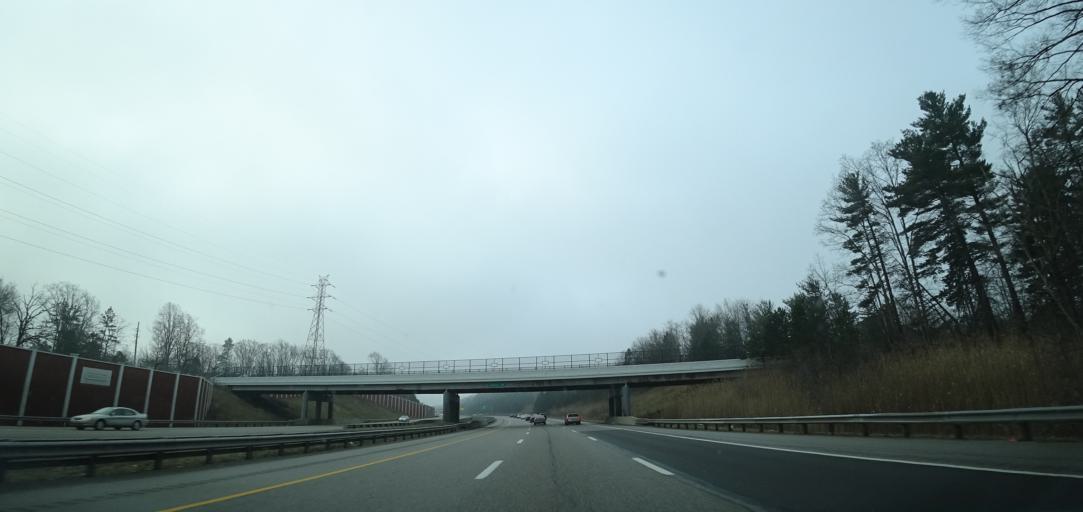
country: US
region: Ohio
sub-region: Cuyahoga County
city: Brecksville
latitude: 41.3086
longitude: -81.6488
